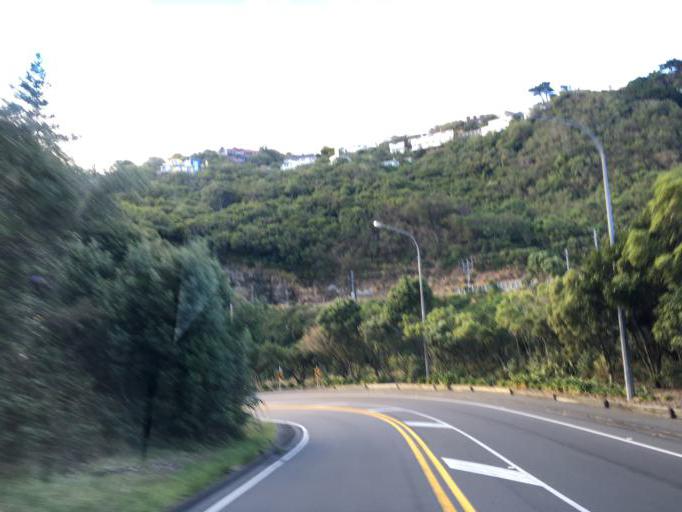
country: NZ
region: Wellington
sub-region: Wellington City
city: Kelburn
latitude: -41.2579
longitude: 174.7810
